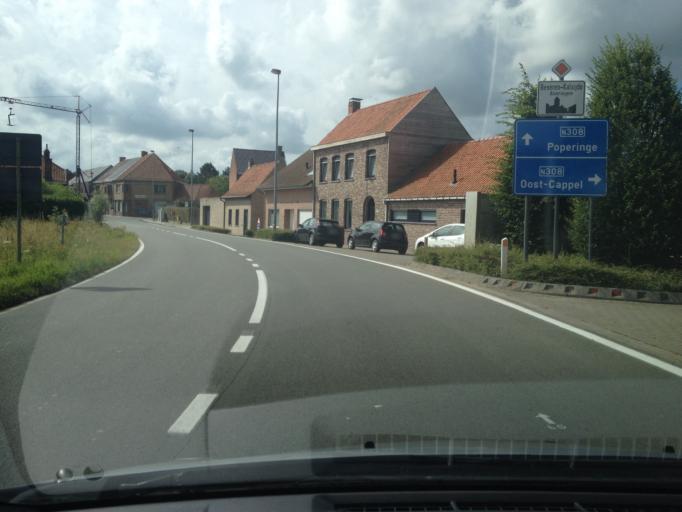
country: FR
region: Nord-Pas-de-Calais
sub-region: Departement du Nord
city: Hondschoote
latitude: 50.9242
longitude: 2.6177
